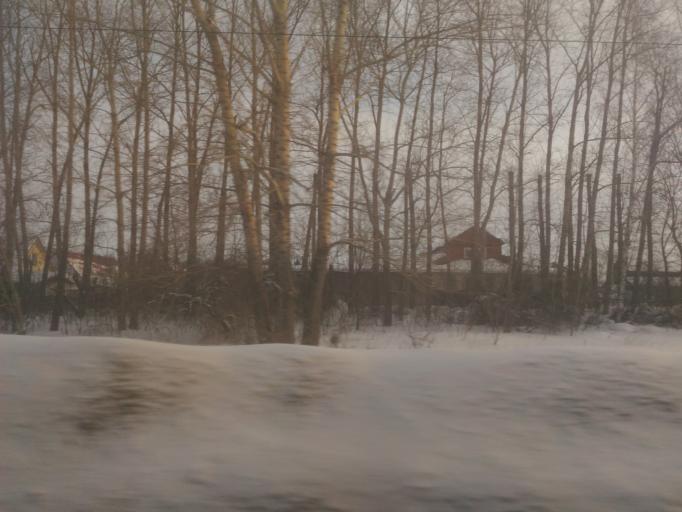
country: RU
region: Ulyanovsk
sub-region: Ulyanovskiy Rayon
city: Ulyanovsk
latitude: 54.3608
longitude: 48.3436
